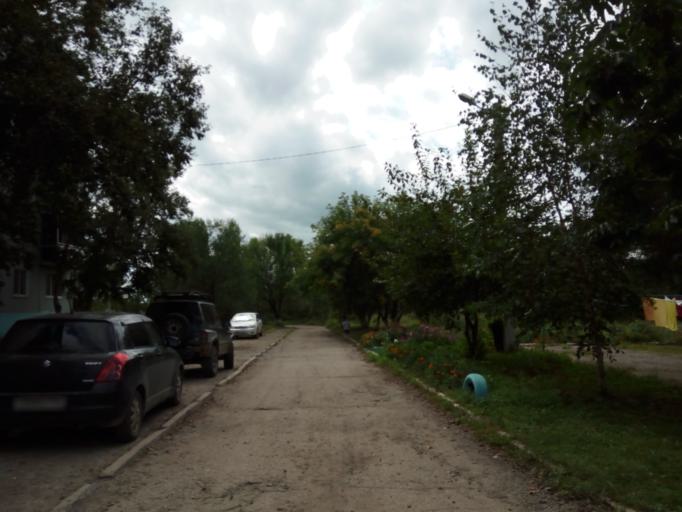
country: RU
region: Primorskiy
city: Dal'nerechensk
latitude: 45.9414
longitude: 133.8145
